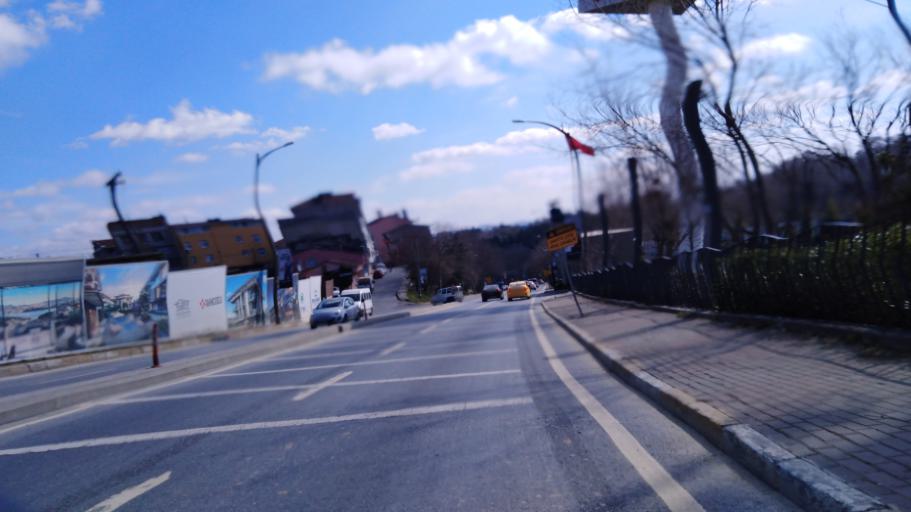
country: TR
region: Istanbul
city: Sisli
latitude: 41.1121
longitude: 29.0449
